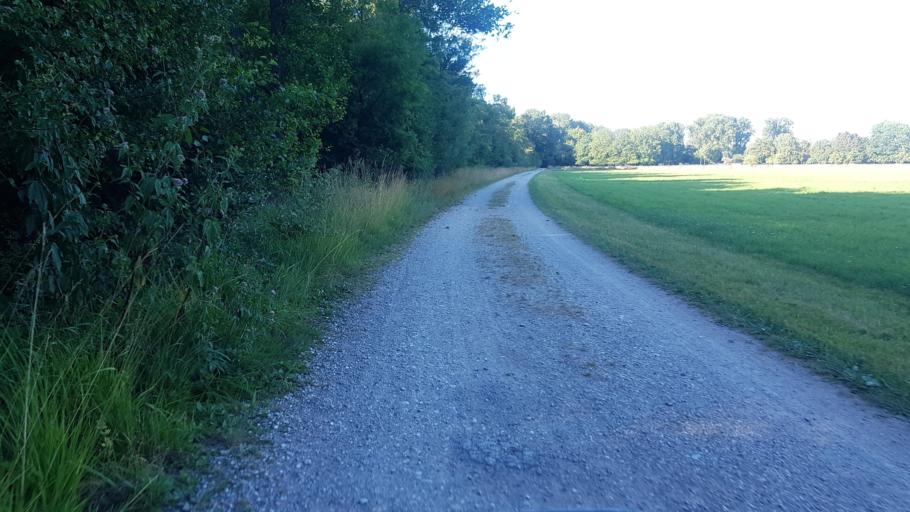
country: DE
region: Bavaria
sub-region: Upper Bavaria
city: Karlsfeld
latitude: 48.2416
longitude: 11.4981
